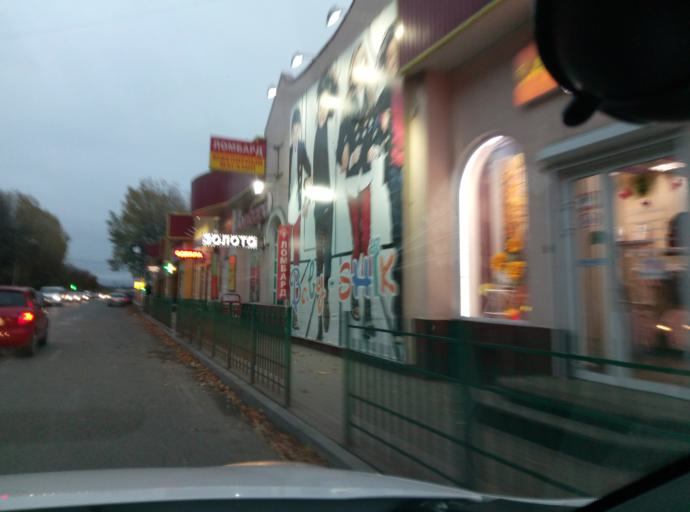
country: RU
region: Stavropol'skiy
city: Yessentukskaya
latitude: 44.0486
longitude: 42.8918
